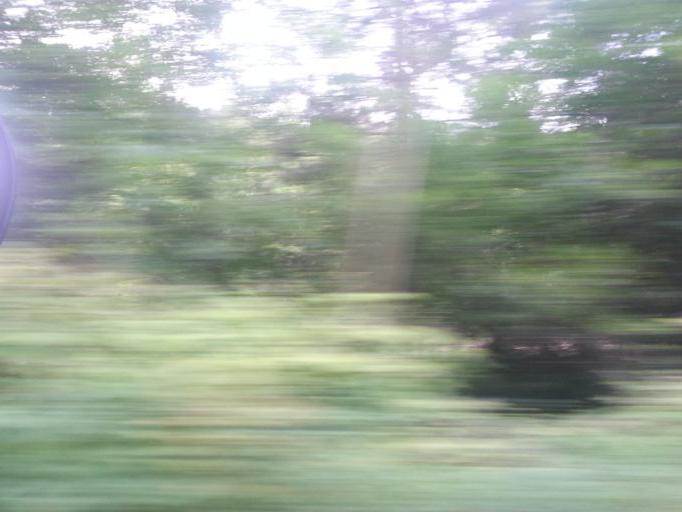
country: US
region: Tennessee
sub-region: Roane County
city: Oliver Springs
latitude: 36.1461
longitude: -84.3866
